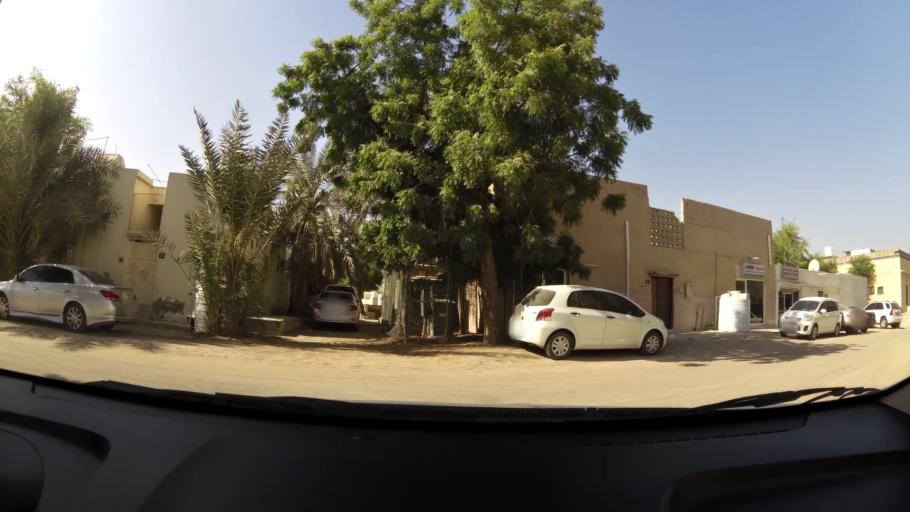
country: AE
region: Ajman
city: Ajman
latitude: 25.4113
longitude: 55.4499
